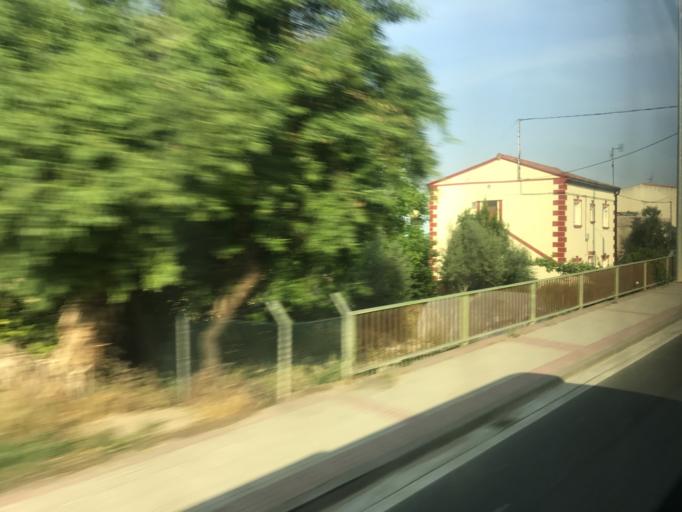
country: ES
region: Castille and Leon
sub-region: Provincia de Burgos
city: Miranda de Ebro
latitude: 42.6947
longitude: -2.9556
